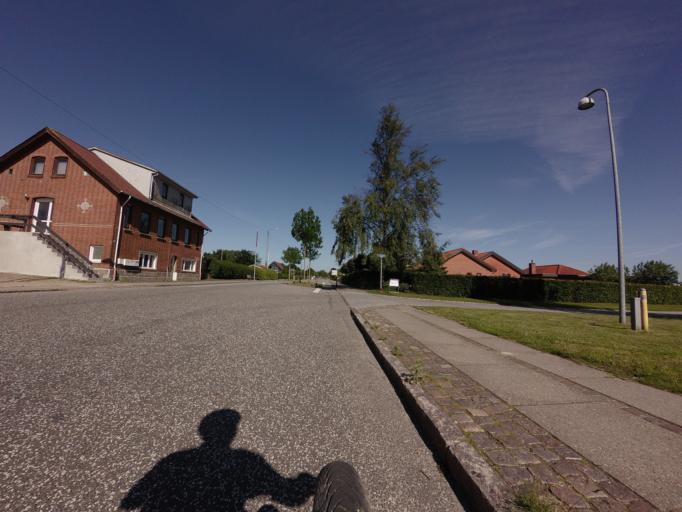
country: DK
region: Central Jutland
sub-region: Horsens Kommune
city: Horsens
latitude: 55.8974
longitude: 9.7594
